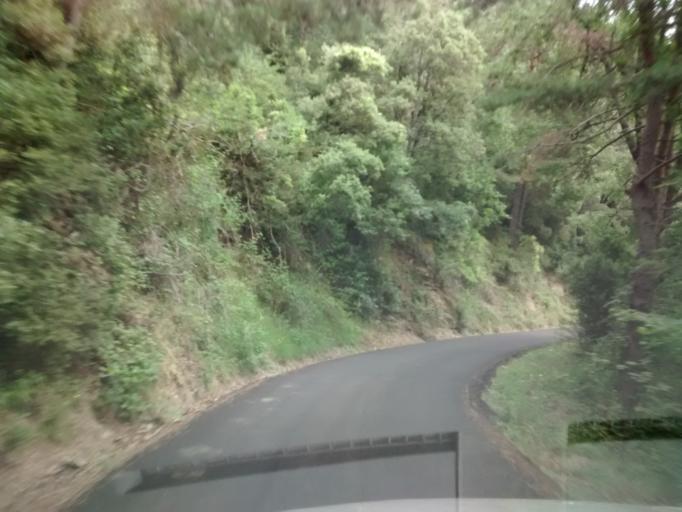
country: ES
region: Aragon
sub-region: Provincia de Huesca
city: Puertolas
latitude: 42.5676
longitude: 0.1393
